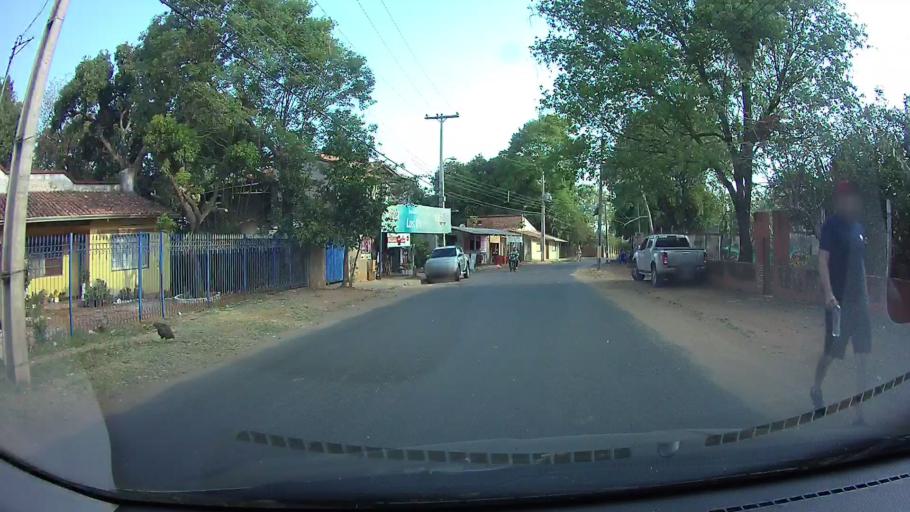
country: PY
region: Central
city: Limpio
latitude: -25.2038
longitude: -57.5068
